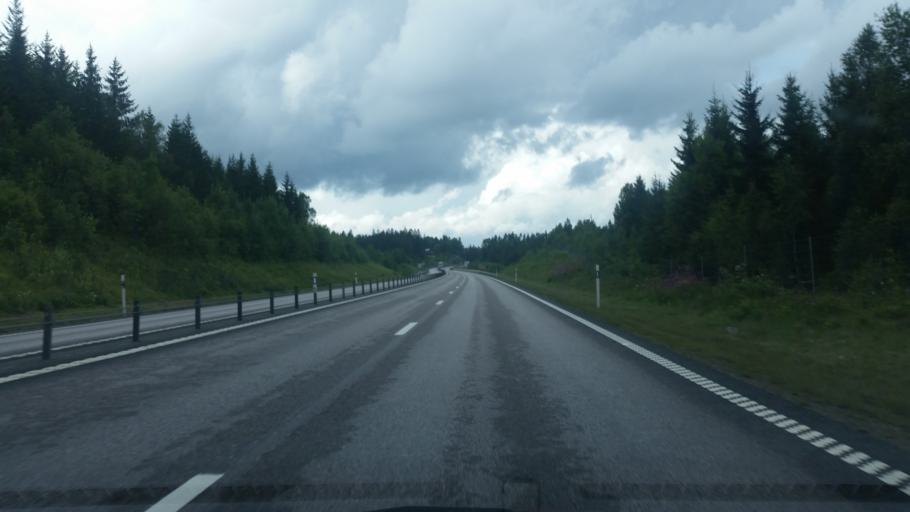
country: SE
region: Vaestra Goetaland
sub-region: Boras Kommun
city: Ganghester
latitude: 57.6551
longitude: 13.0518
